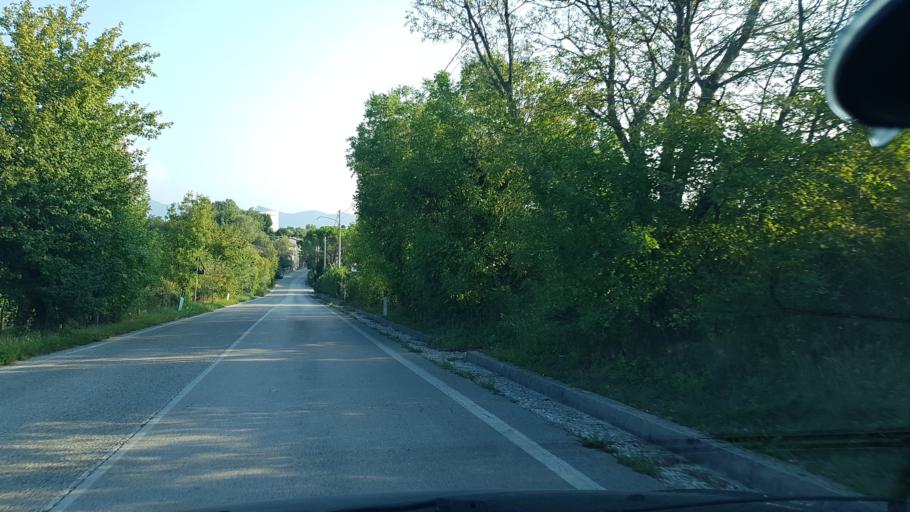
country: IT
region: Friuli Venezia Giulia
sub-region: Provincia di Gorizia
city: San Floriano del Collio
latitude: 45.9743
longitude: 13.6116
